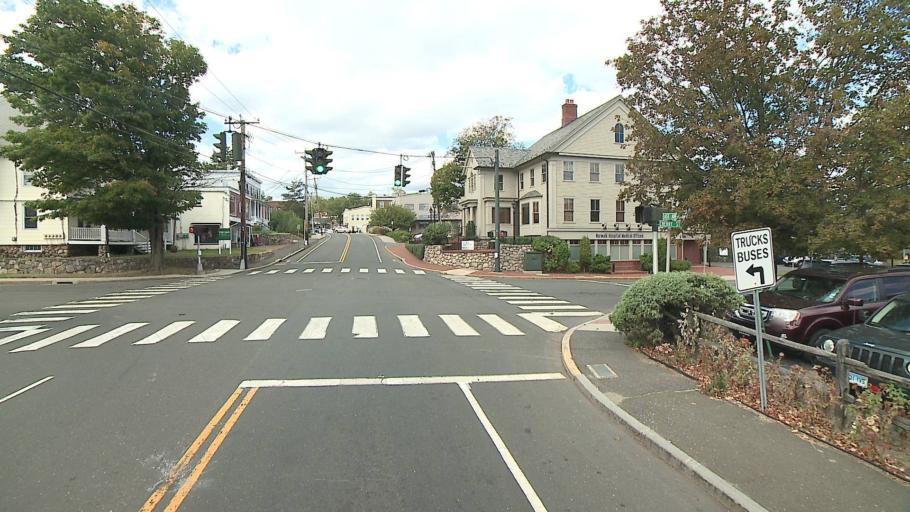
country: US
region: Connecticut
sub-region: Fairfield County
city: New Canaan
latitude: 41.1477
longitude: -73.4903
